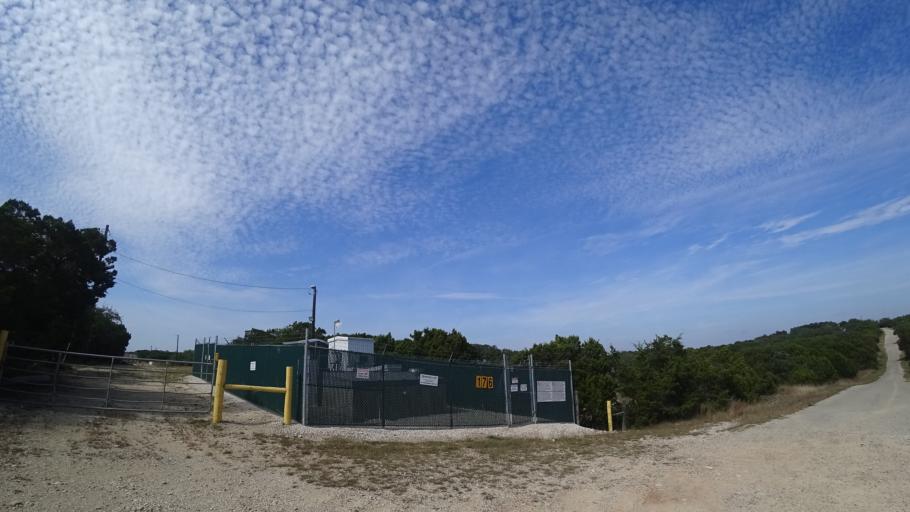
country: US
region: Texas
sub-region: Travis County
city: Shady Hollow
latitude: 30.2179
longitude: -97.9248
